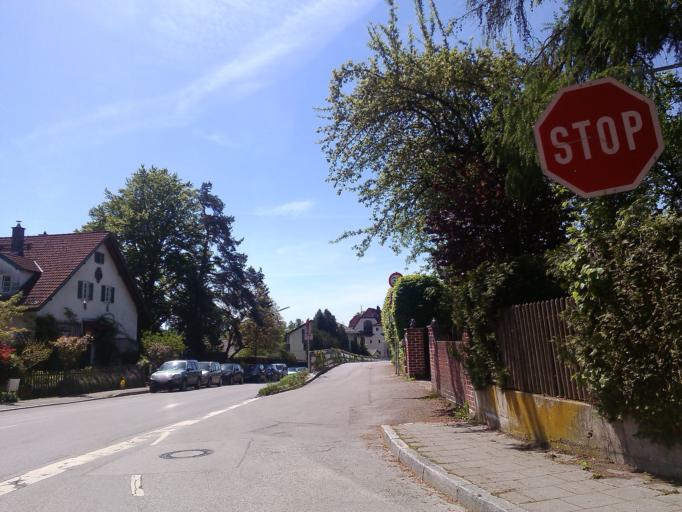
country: DE
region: Bavaria
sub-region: Upper Bavaria
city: Starnberg
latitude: 47.9943
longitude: 11.3385
